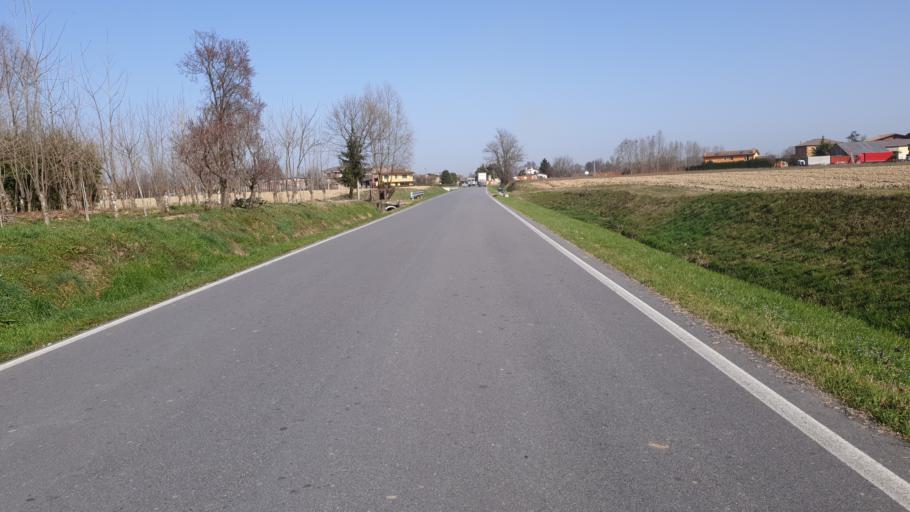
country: IT
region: Veneto
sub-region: Provincia di Padova
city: Cavino
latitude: 45.5099
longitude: 11.8908
